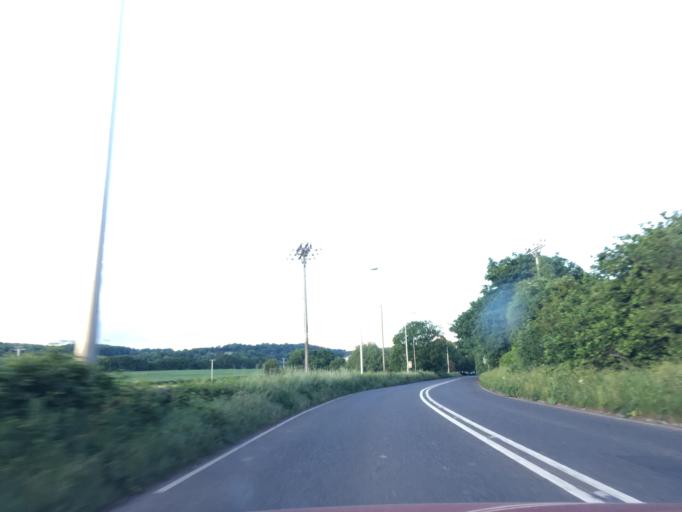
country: GB
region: England
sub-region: North Somerset
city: Wrington
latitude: 51.3536
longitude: -2.7459
